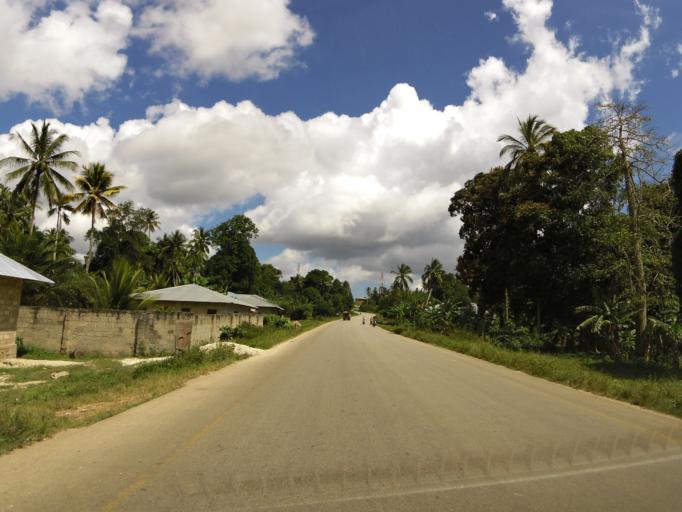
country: TZ
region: Zanzibar Central/South
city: Koani
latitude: -6.1354
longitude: 39.2924
